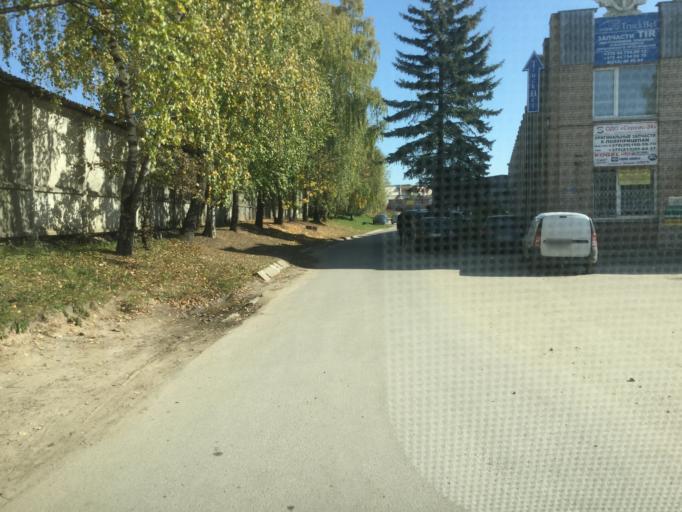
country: BY
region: Vitebsk
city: Vitebsk
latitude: 55.1819
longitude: 30.2520
